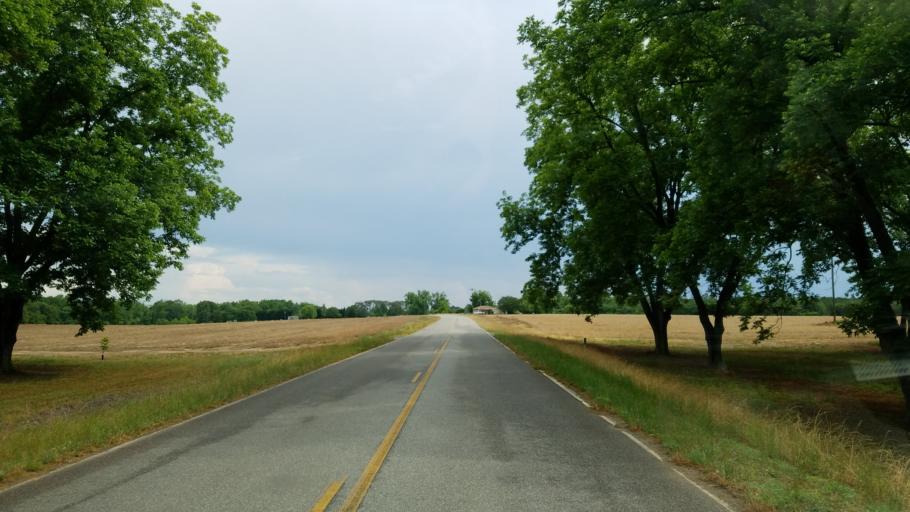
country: US
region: Georgia
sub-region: Dooly County
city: Unadilla
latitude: 32.3052
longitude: -83.7913
